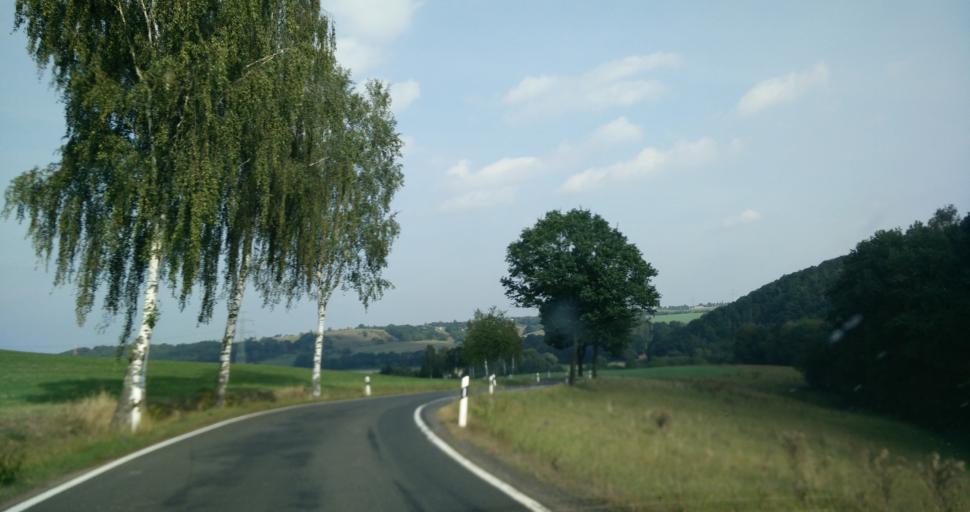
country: DE
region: Saxony
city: Colditz
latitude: 51.1034
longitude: 12.8015
